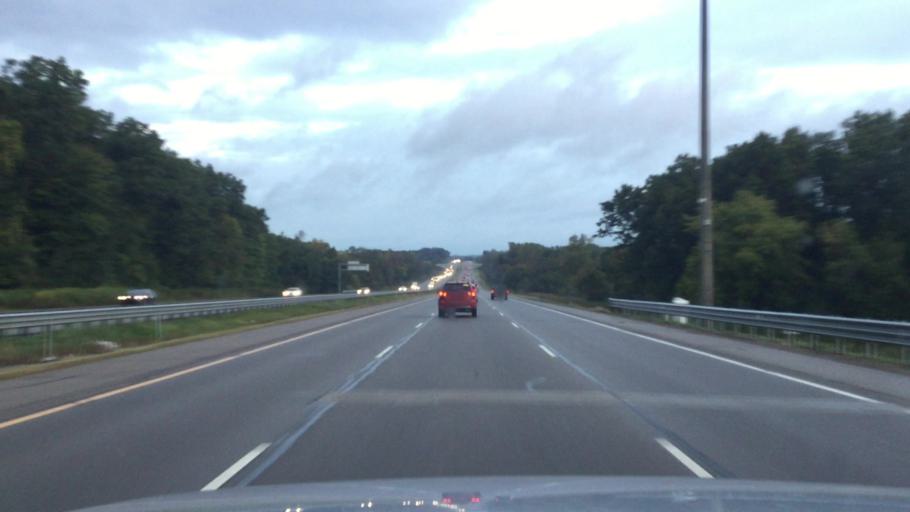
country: US
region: Michigan
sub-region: Oakland County
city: Holly
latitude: 42.8329
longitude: -83.5775
